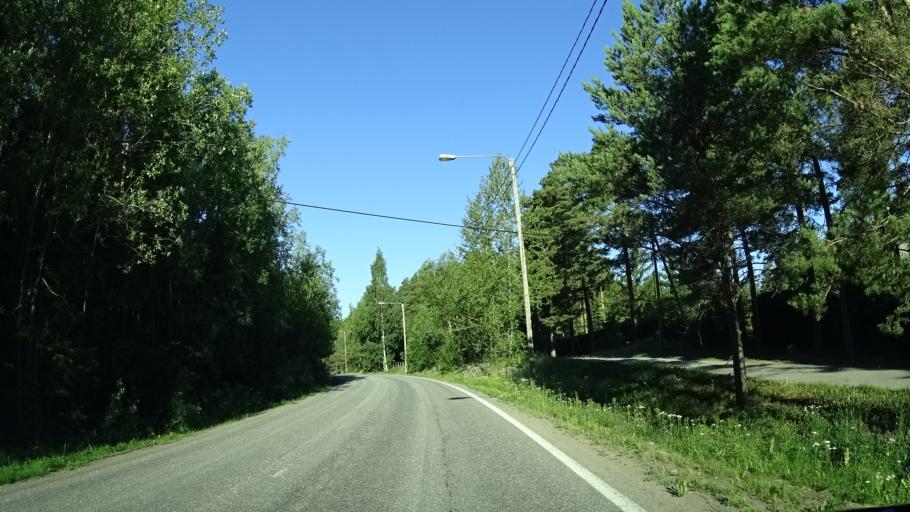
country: FI
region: Varsinais-Suomi
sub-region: Turku
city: Merimasku
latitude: 60.4595
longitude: 21.9055
